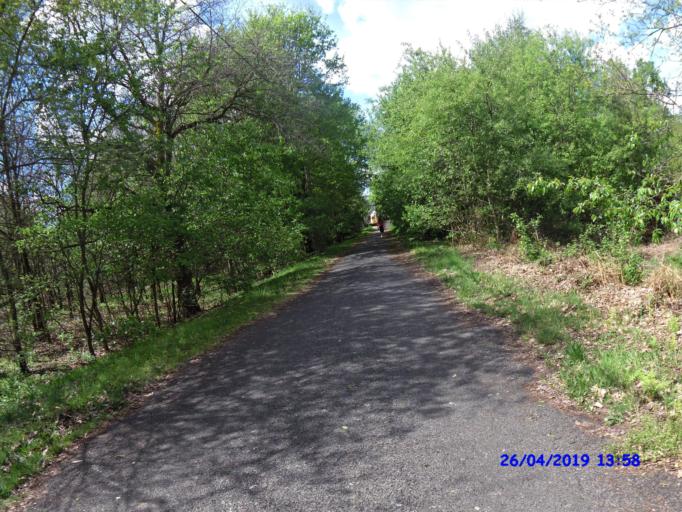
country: BE
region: Flanders
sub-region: Provincie Limburg
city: Heusden
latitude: 51.0384
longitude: 5.2840
